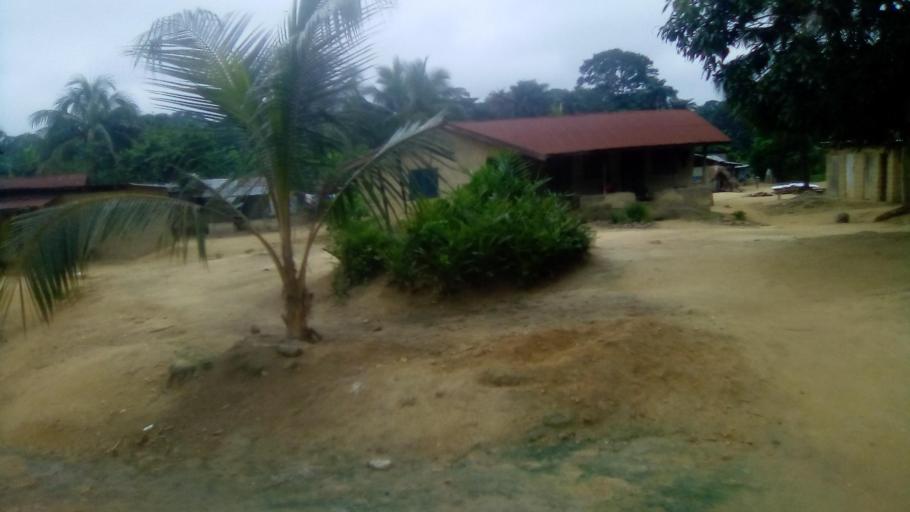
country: SL
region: Eastern Province
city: Kailahun
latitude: 8.2957
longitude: -10.6072
